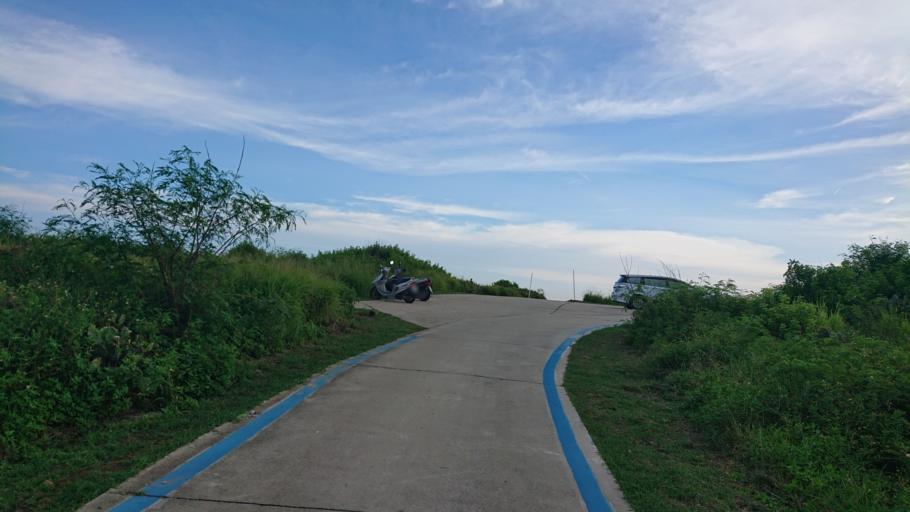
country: TW
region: Taiwan
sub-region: Penghu
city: Ma-kung
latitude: 23.5196
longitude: 119.6099
